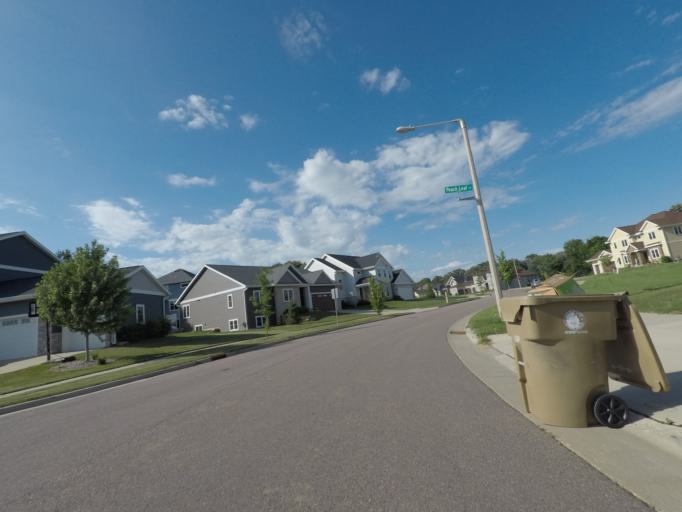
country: US
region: Wisconsin
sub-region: Dane County
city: Middleton
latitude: 43.0738
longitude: -89.5574
